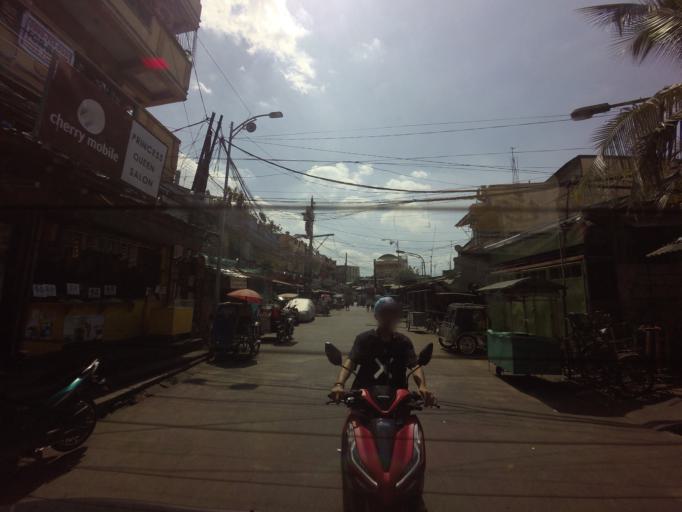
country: PH
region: Metro Manila
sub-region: City of Manila
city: Manila
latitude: 14.6207
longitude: 120.9615
